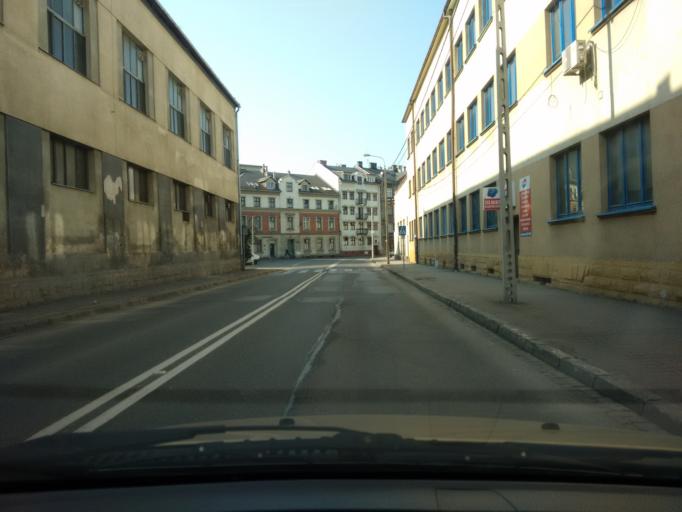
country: PL
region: Silesian Voivodeship
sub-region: Bielsko-Biala
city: Bielsko-Biala
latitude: 49.8317
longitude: 19.0498
